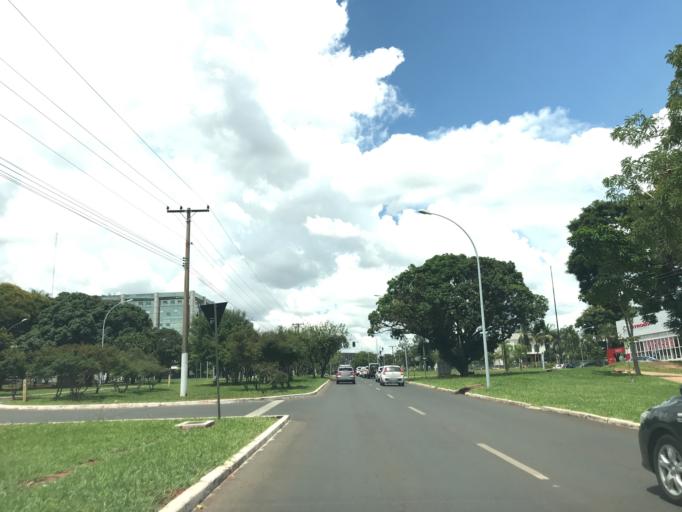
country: BR
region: Federal District
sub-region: Brasilia
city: Brasilia
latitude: -15.7834
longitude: -47.8861
